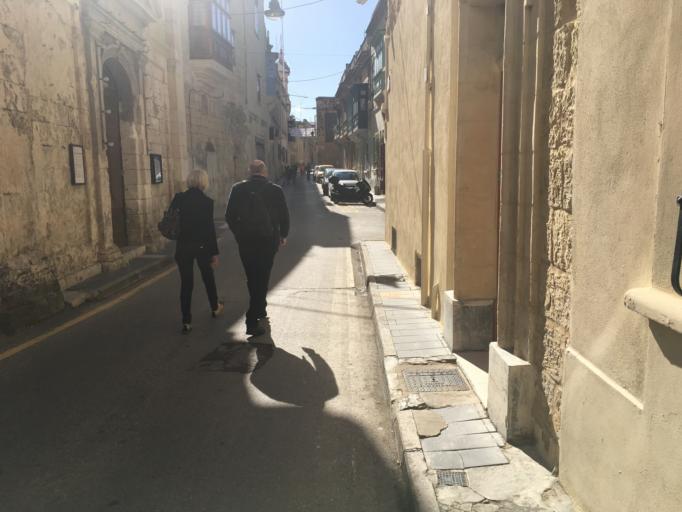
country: MT
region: Ir-Rabat
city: Rabat
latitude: 35.8843
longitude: 14.4001
